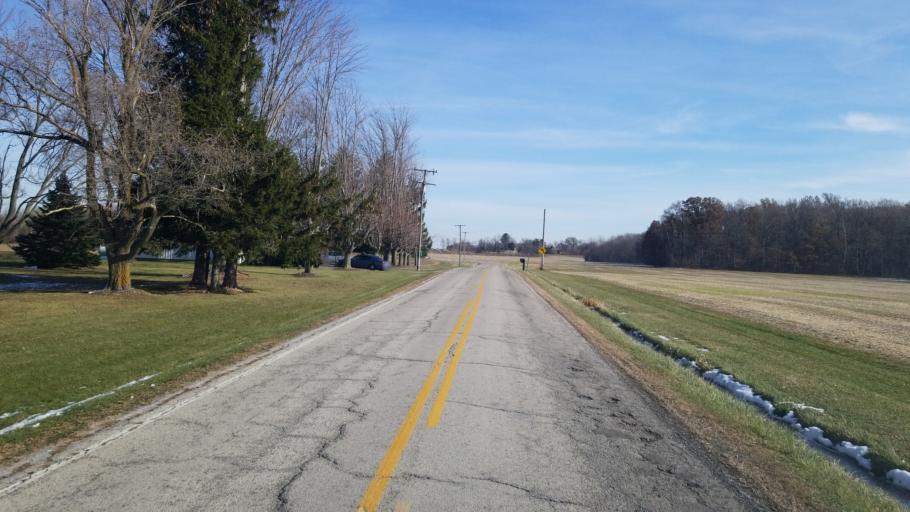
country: US
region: Ohio
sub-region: Huron County
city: Wakeman
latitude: 41.1975
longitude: -82.4657
